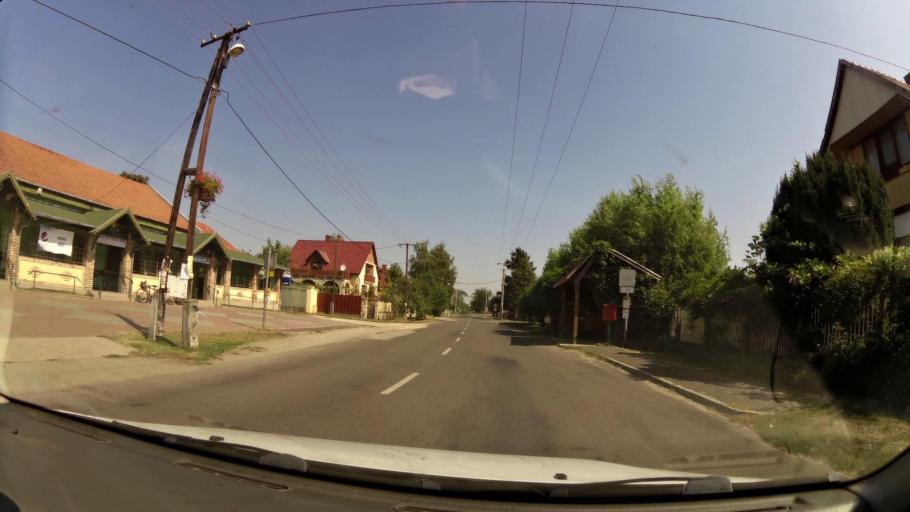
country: HU
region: Pest
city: Ujszilvas
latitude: 47.2769
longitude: 19.9228
